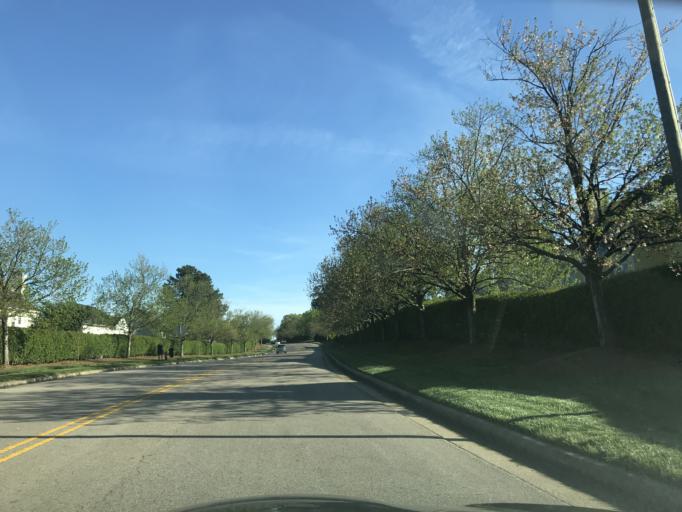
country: US
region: North Carolina
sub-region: Wake County
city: Knightdale
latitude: 35.8363
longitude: -78.5614
